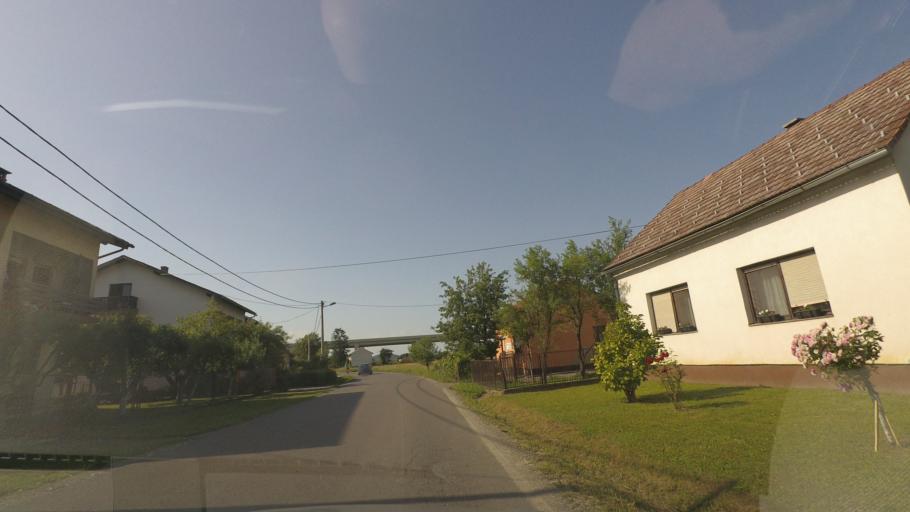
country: HR
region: Karlovacka
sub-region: Grad Karlovac
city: Karlovac
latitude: 45.5086
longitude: 15.5312
